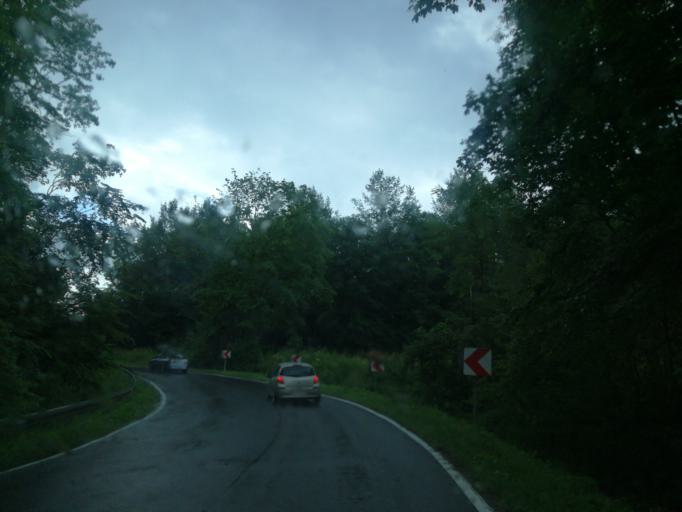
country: PL
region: Subcarpathian Voivodeship
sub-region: Powiat leski
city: Polanczyk
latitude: 49.4048
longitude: 22.4573
